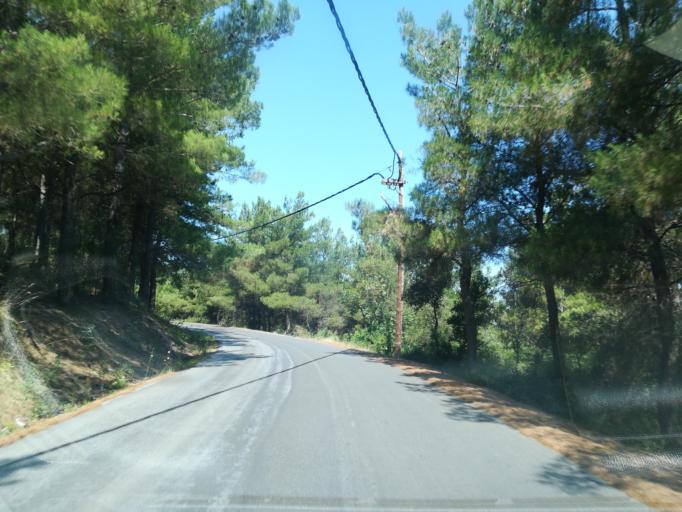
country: GR
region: Central Macedonia
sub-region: Nomos Thessalonikis
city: Asvestochori
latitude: 40.6406
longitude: 23.0099
